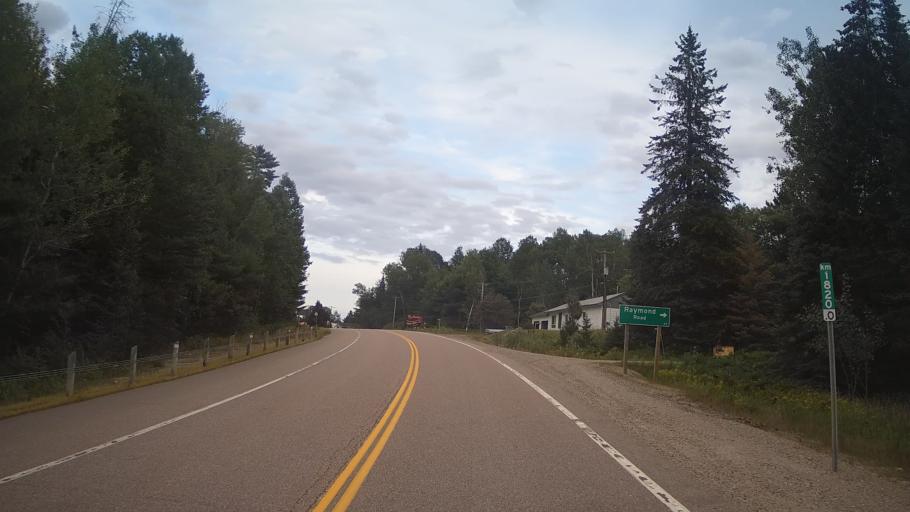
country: CA
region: Ontario
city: Deep River
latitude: 46.1719
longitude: -77.7035
